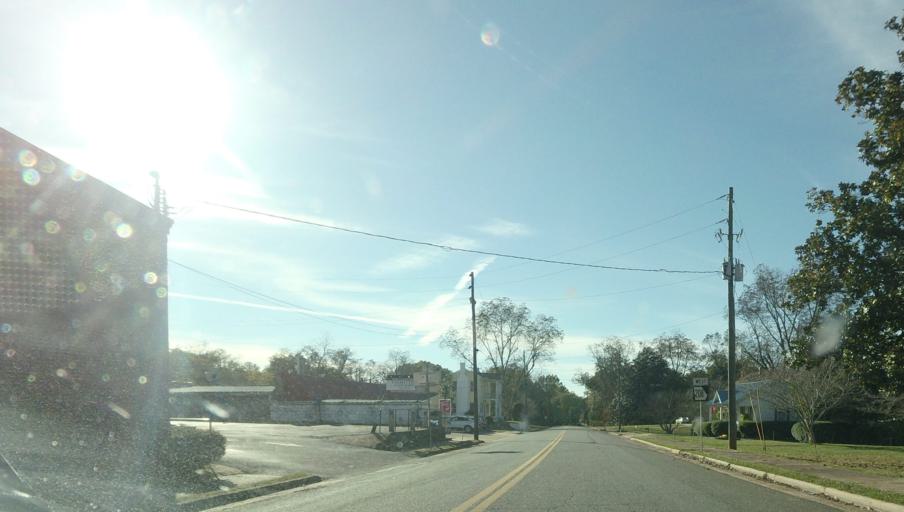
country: US
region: Georgia
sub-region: Talbot County
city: Talbotton
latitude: 32.6777
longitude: -84.5414
